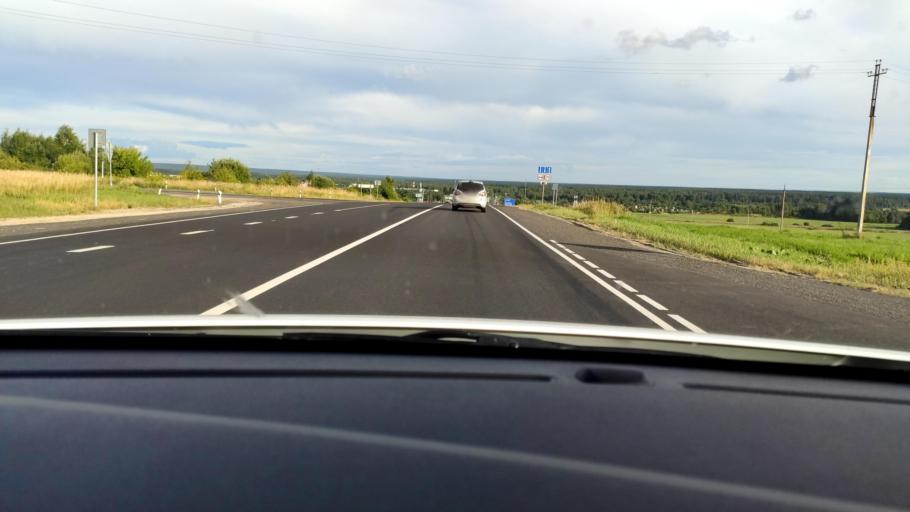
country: RU
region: Mariy-El
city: Krasnogorskiy
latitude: 56.1740
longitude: 48.2766
